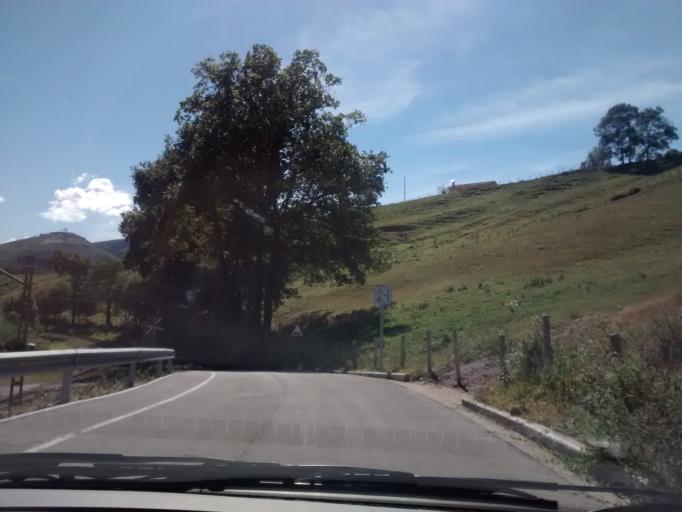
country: ES
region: Cantabria
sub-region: Provincia de Cantabria
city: Lierganes
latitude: 43.3552
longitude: -3.7127
